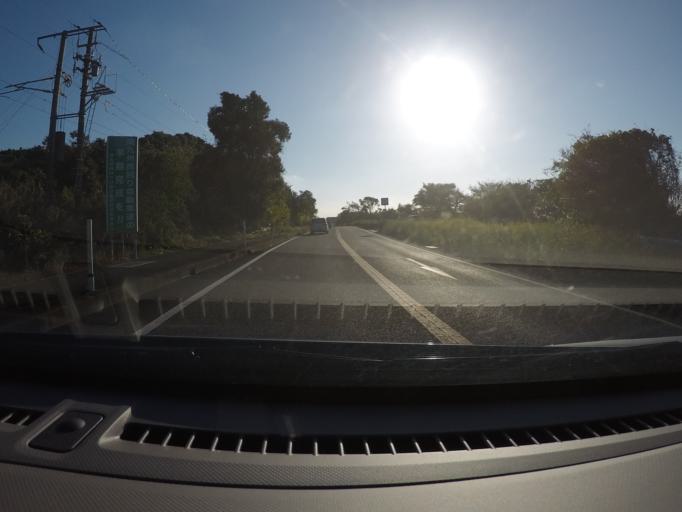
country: JP
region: Kagoshima
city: Izumi
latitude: 32.1353
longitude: 130.3523
